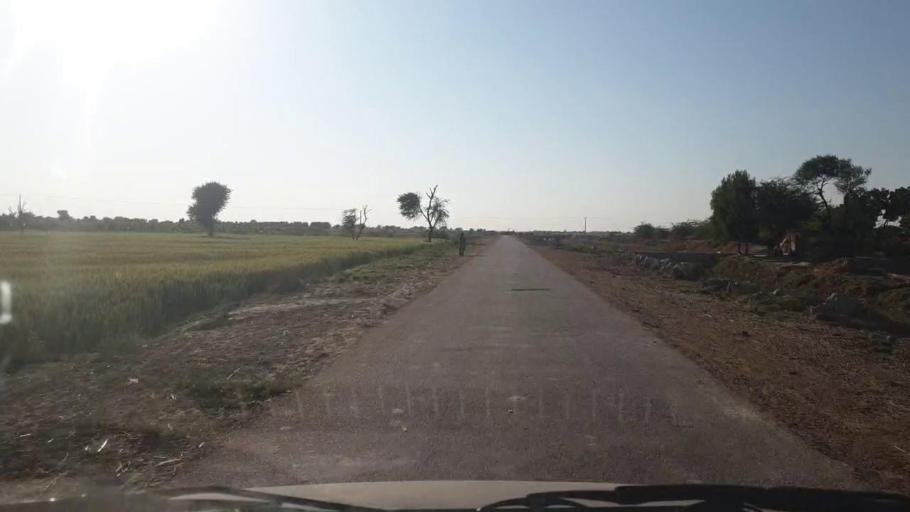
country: PK
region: Sindh
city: Samaro
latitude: 25.3517
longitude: 69.2957
